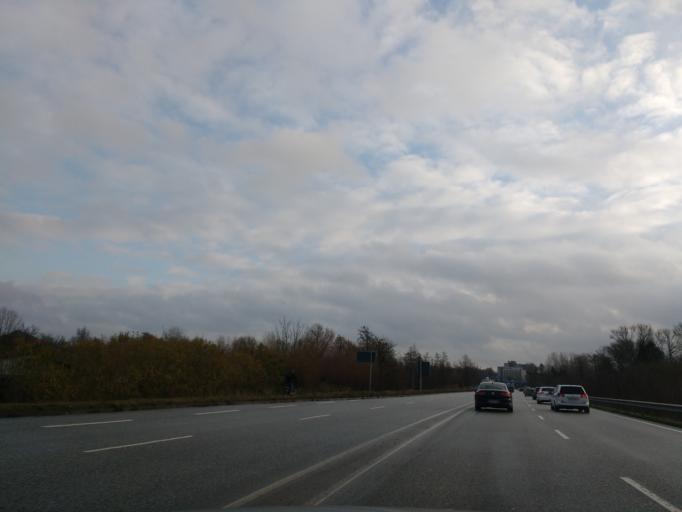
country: DE
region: Schleswig-Holstein
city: Eckernforde
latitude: 54.4688
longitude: 9.8302
